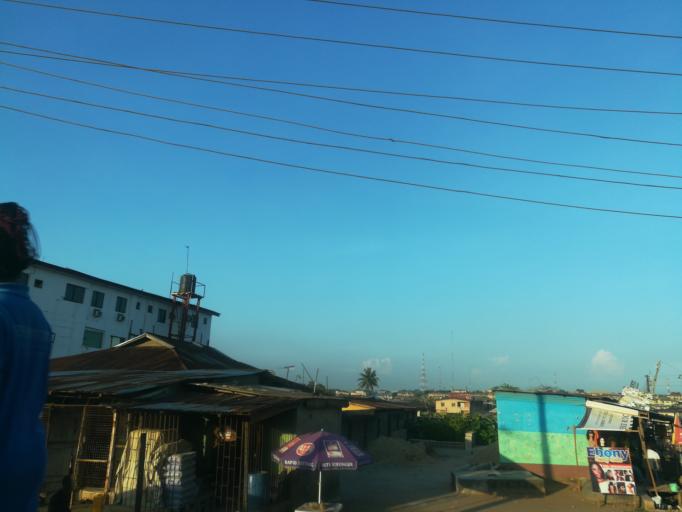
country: NG
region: Lagos
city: Ikorodu
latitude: 6.6176
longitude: 3.5086
